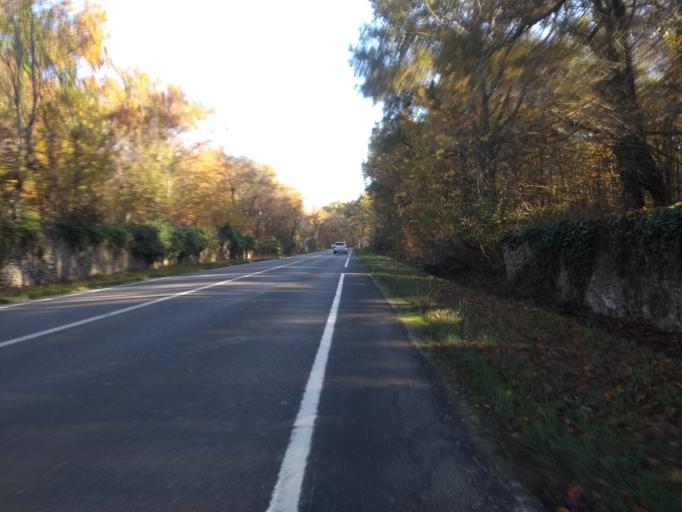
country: FR
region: Aquitaine
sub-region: Departement de la Gironde
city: Ayguemorte-les-Graves
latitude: 44.6934
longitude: -0.5074
